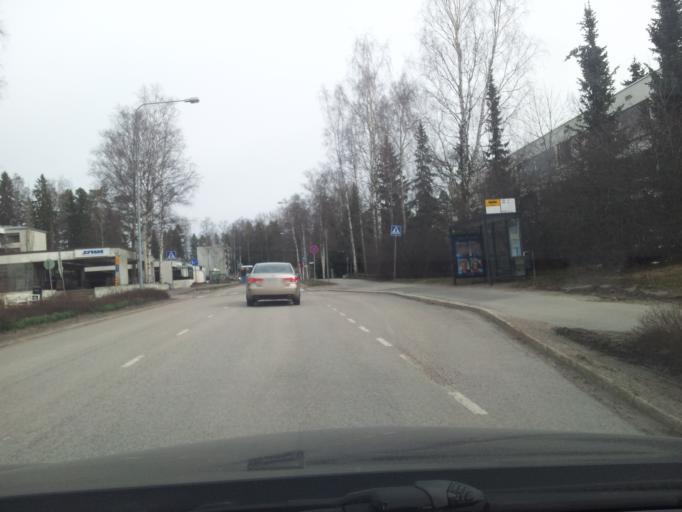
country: FI
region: Uusimaa
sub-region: Helsinki
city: Otaniemi
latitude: 60.1866
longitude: 24.7967
